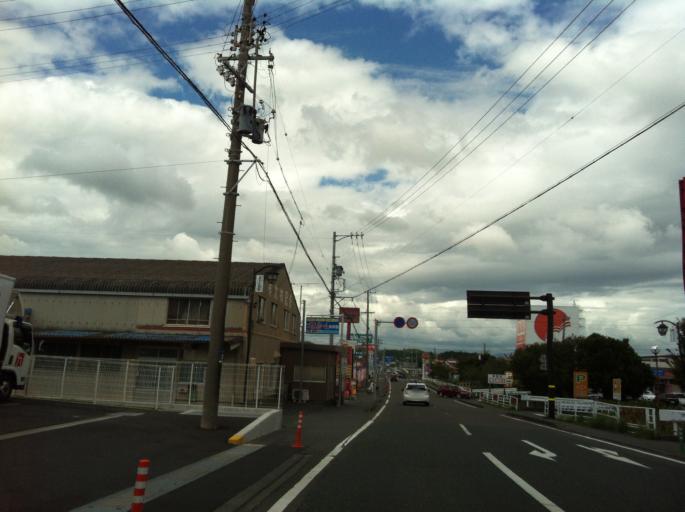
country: JP
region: Shizuoka
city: Kakegawa
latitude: 34.6702
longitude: 138.0454
